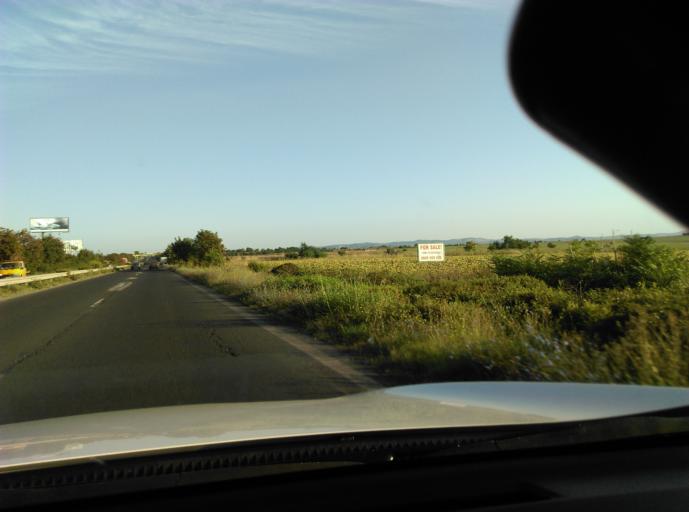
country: BG
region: Burgas
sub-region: Obshtina Burgas
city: Burgas
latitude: 42.5421
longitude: 27.4394
